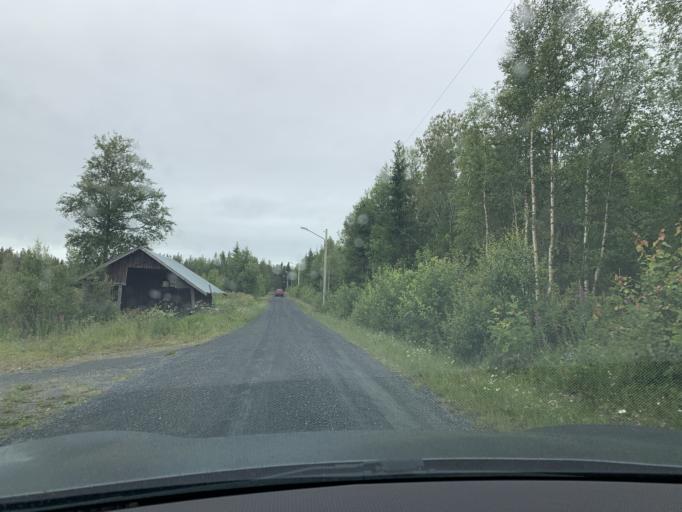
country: SE
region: Jaemtland
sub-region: Krokoms Kommun
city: Valla
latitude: 63.2369
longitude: 14.0124
